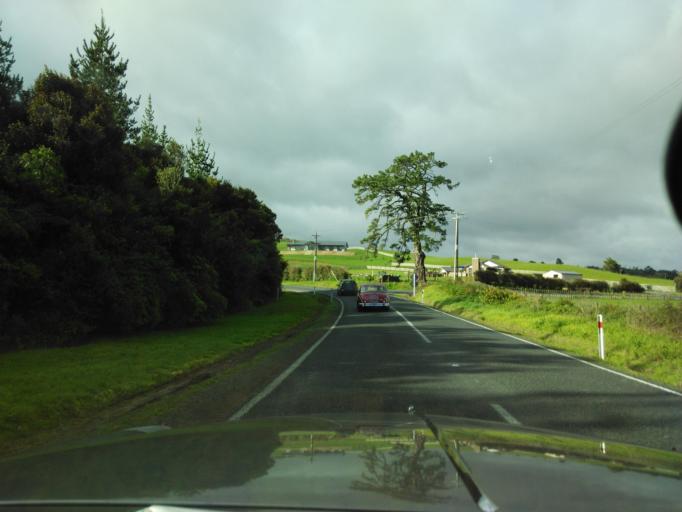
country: NZ
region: Auckland
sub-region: Auckland
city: Pukekohe East
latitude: -37.1456
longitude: 175.0194
